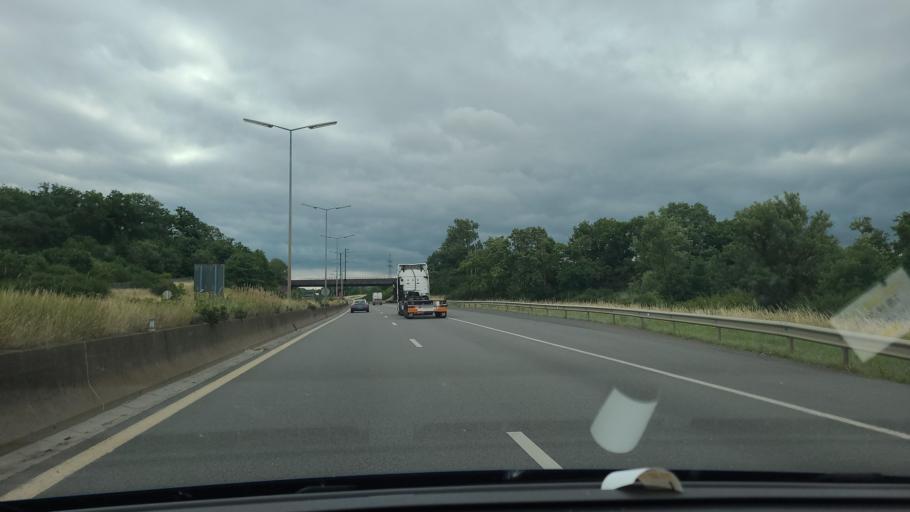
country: LU
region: Luxembourg
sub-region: Canton de Capellen
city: Bascharage
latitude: 49.5567
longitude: 5.9018
